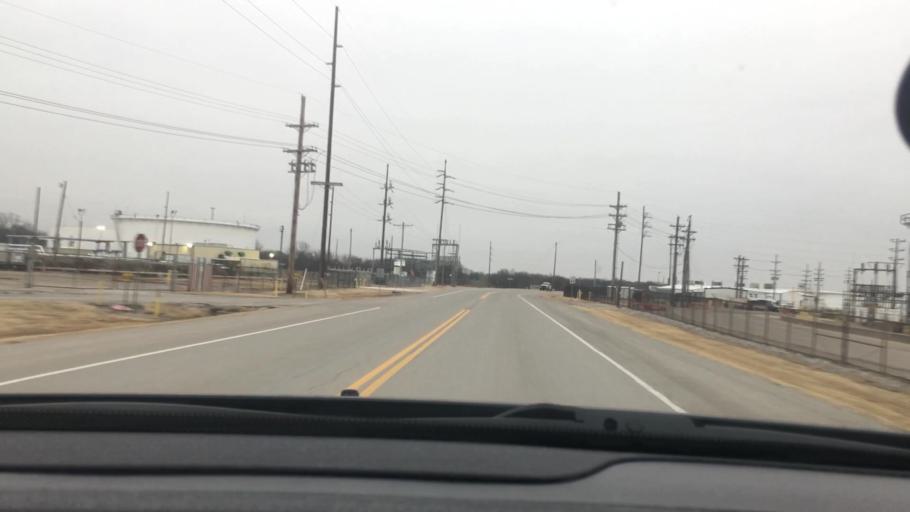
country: US
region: Oklahoma
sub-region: Garvin County
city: Wynnewood
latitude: 34.6336
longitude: -97.1677
